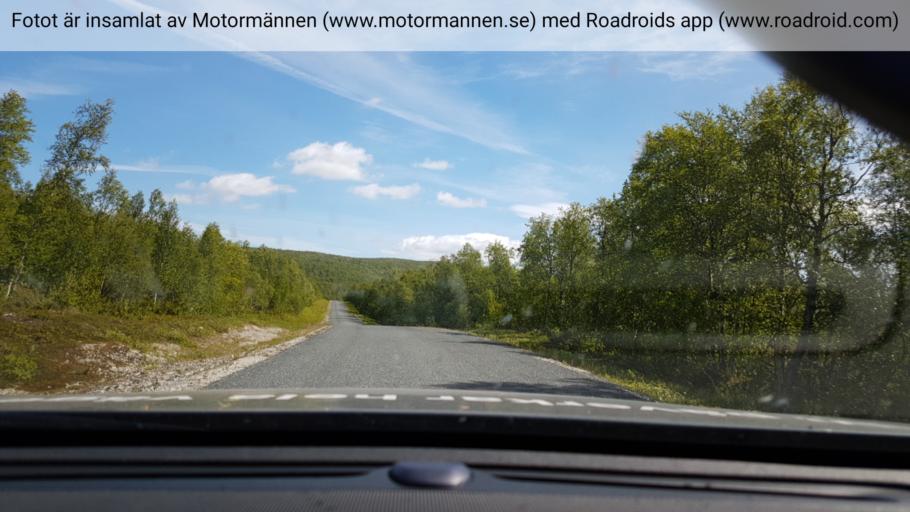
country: SE
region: Vaesterbotten
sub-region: Vilhelmina Kommun
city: Sjoberg
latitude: 65.3313
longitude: 15.1587
